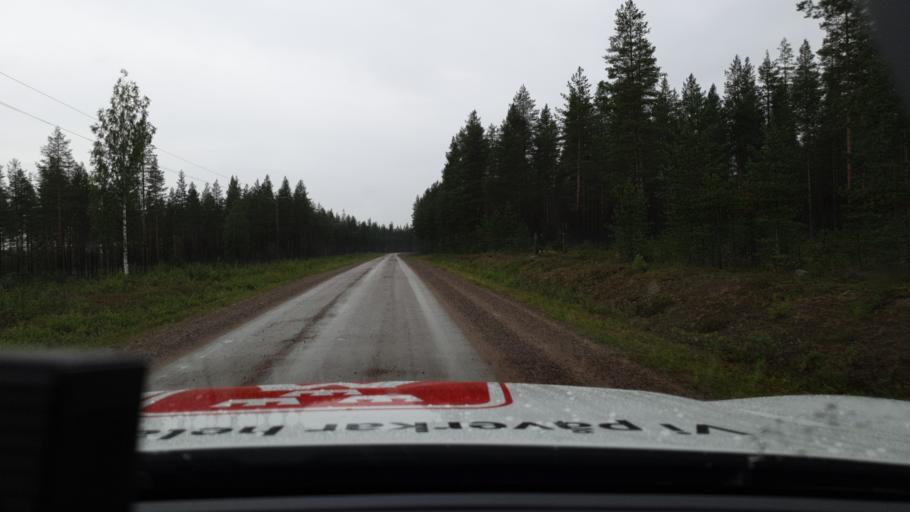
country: SE
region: Norrbotten
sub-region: Bodens Kommun
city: Boden
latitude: 66.3013
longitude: 21.3246
